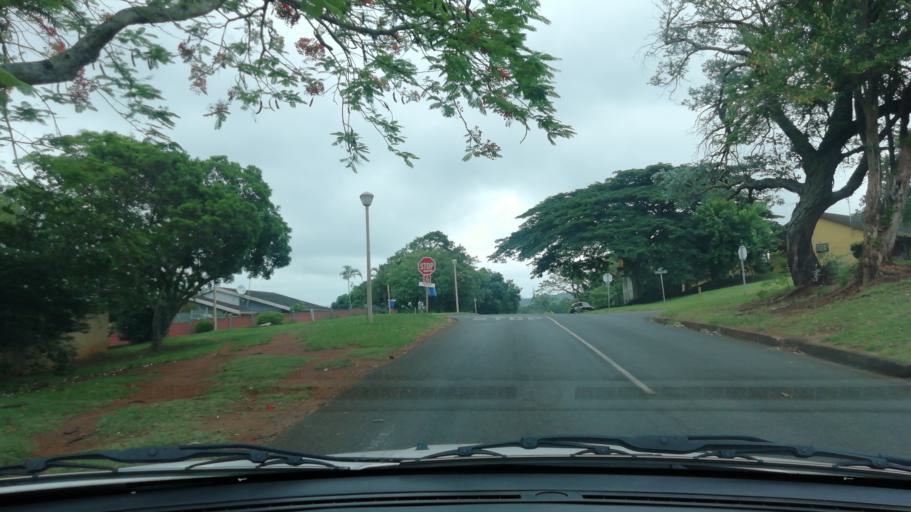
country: ZA
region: KwaZulu-Natal
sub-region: uThungulu District Municipality
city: Empangeni
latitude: -28.7575
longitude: 31.8879
